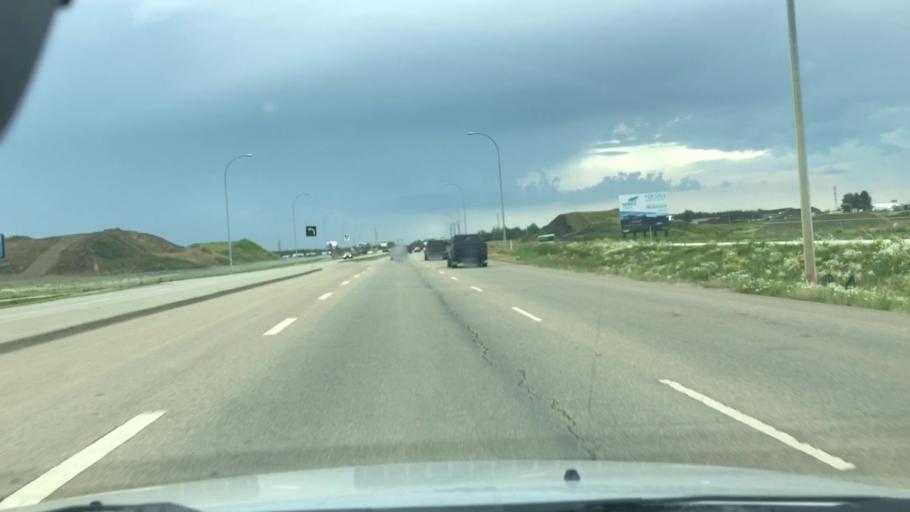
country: CA
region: Alberta
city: St. Albert
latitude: 53.5994
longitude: -113.6072
